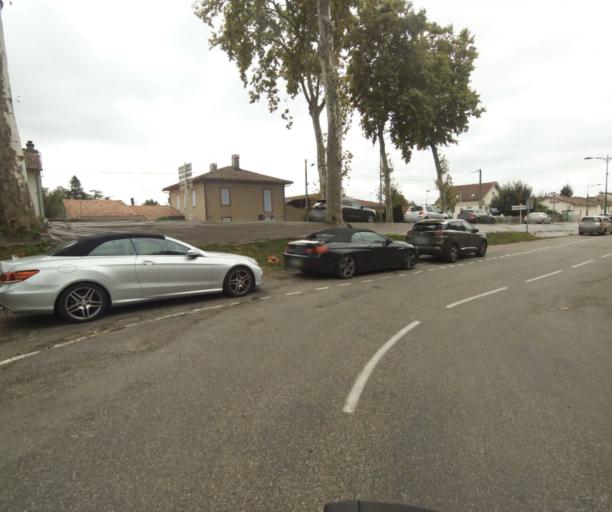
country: FR
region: Midi-Pyrenees
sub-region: Departement du Tarn-et-Garonne
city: Montech
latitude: 43.9596
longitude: 1.2365
